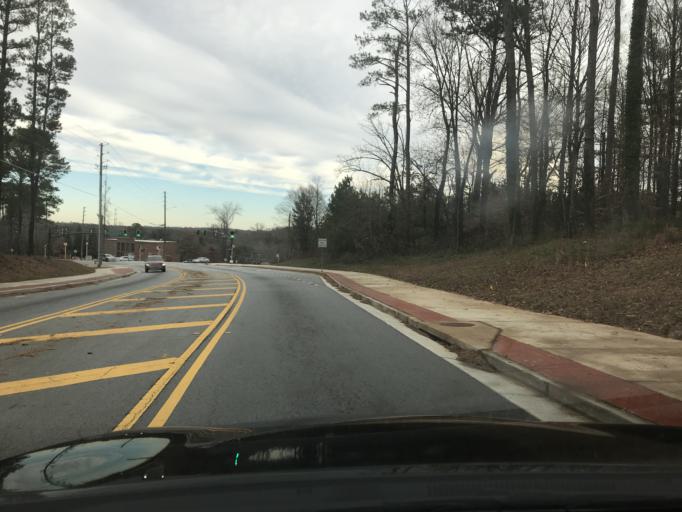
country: US
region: Georgia
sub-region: Fulton County
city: East Point
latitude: 33.7192
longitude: -84.5079
